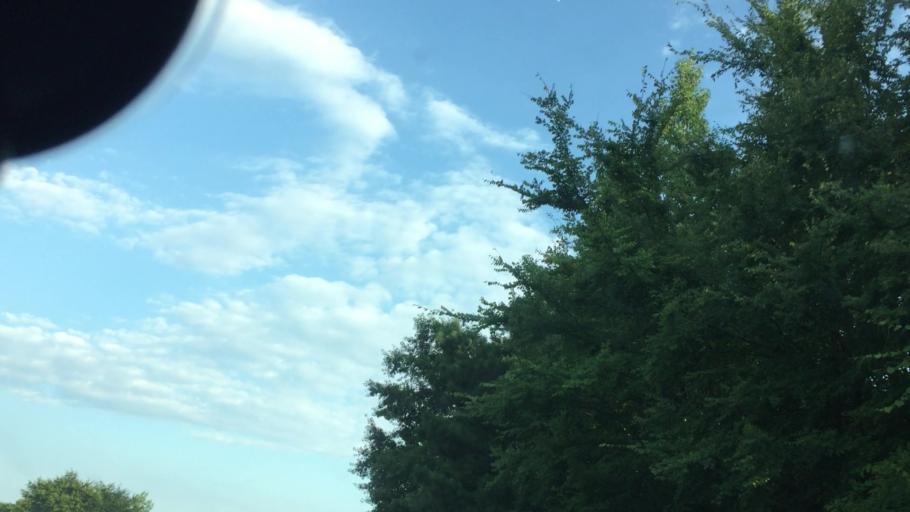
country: US
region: Georgia
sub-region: DeKalb County
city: Pine Mountain
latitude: 33.6545
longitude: -84.1884
